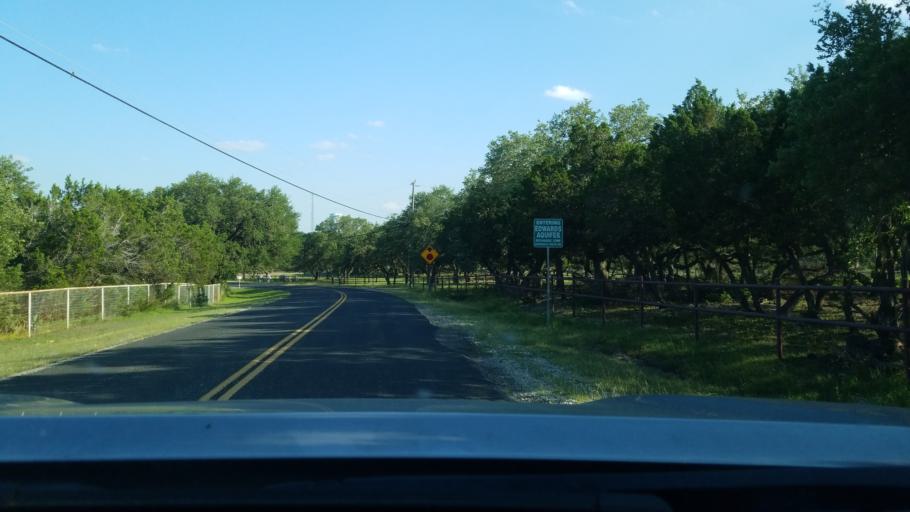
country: US
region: Texas
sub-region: Bexar County
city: Timberwood Park
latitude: 29.6994
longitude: -98.4366
